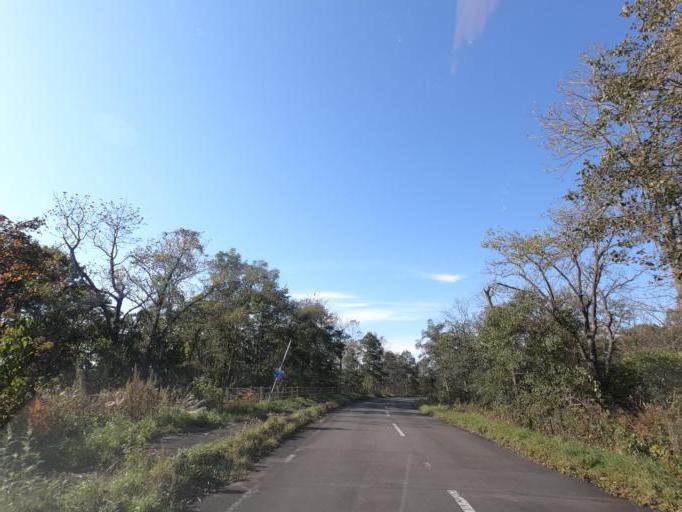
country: JP
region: Hokkaido
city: Obihiro
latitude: 42.6093
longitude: 143.5460
